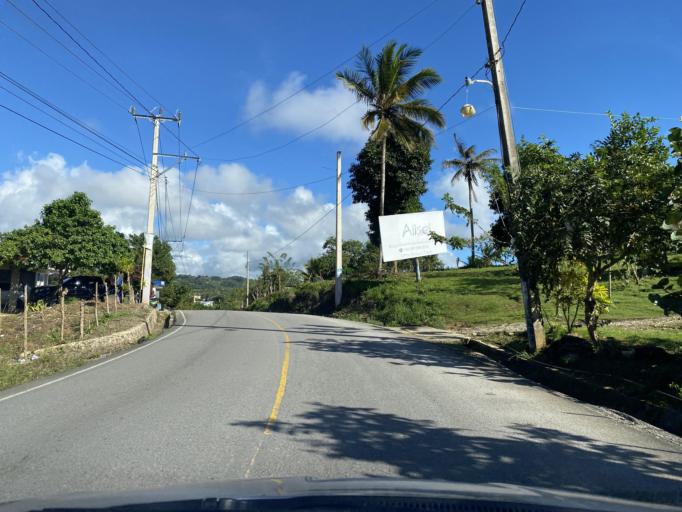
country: DO
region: Samana
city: Sanchez
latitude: 19.2508
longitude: -69.5854
